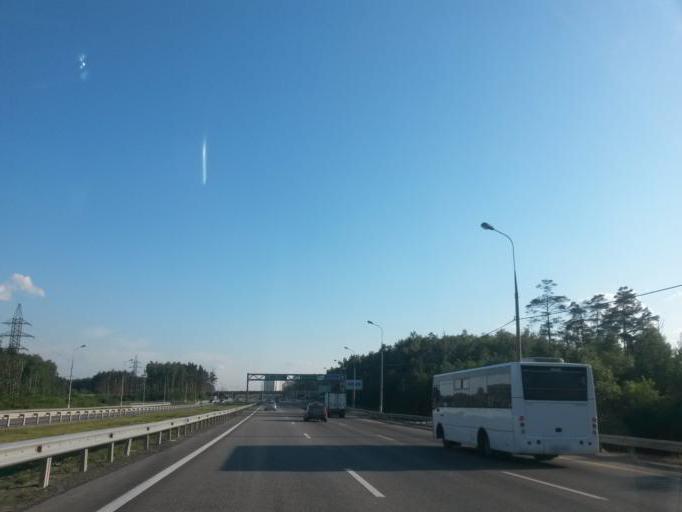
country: RU
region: Moskovskaya
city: Vostryakovo
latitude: 55.4094
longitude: 37.7894
